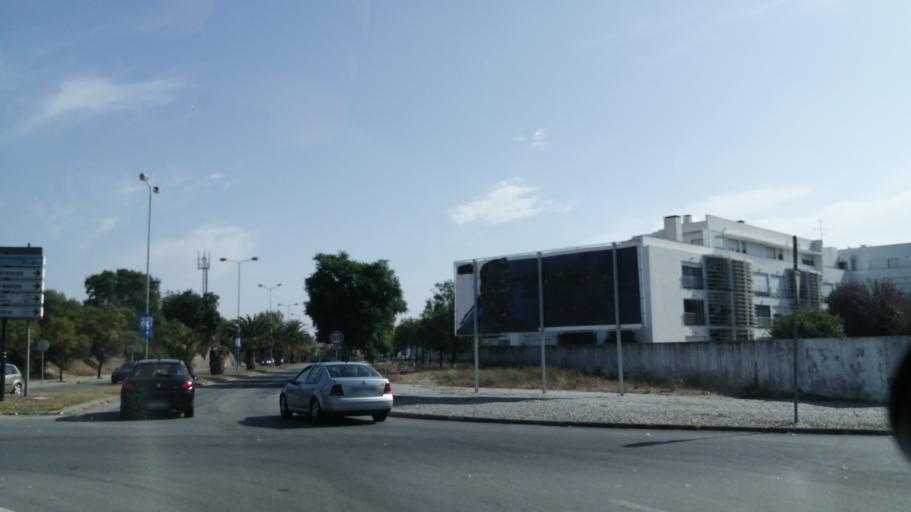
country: PT
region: Evora
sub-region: Evora
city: Evora
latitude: 38.5649
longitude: -7.9278
